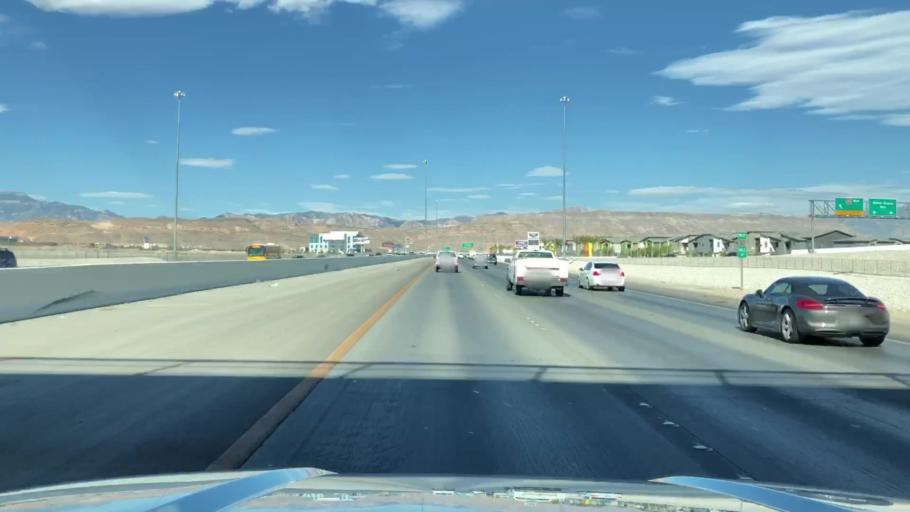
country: US
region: Nevada
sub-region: Clark County
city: Spring Valley
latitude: 36.0663
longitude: -115.2610
